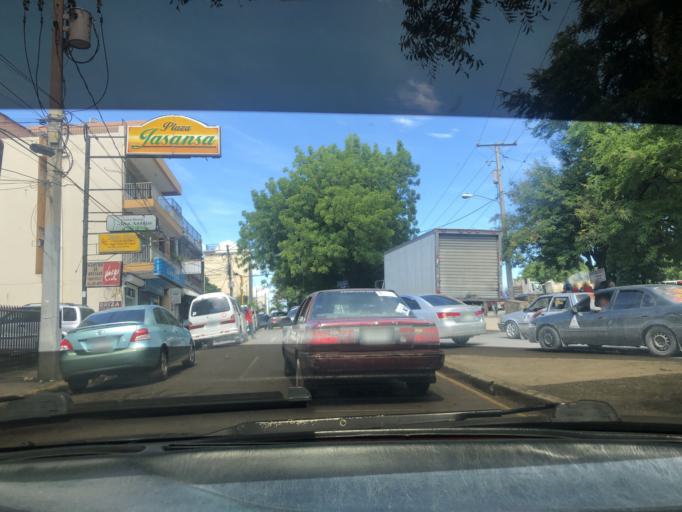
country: DO
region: Santiago
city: Santiago de los Caballeros
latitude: 19.4498
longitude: -70.7088
